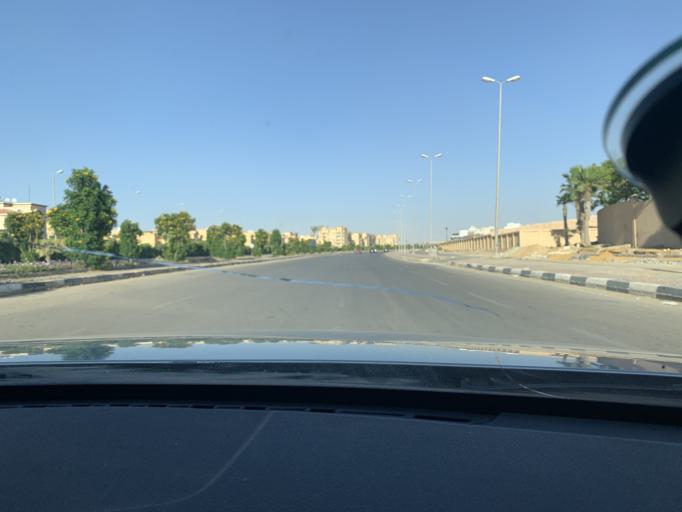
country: EG
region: Muhafazat al Qalyubiyah
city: Al Khankah
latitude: 30.0532
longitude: 31.5012
